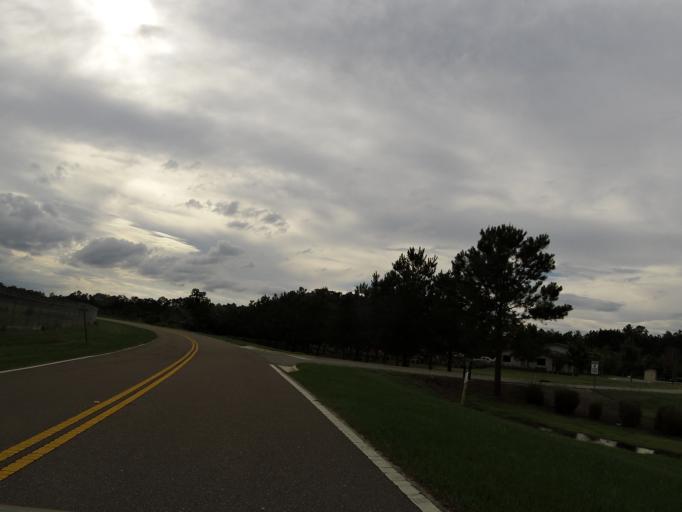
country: US
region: Florida
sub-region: Nassau County
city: Nassau Village-Ratliff
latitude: 30.5467
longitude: -81.7229
